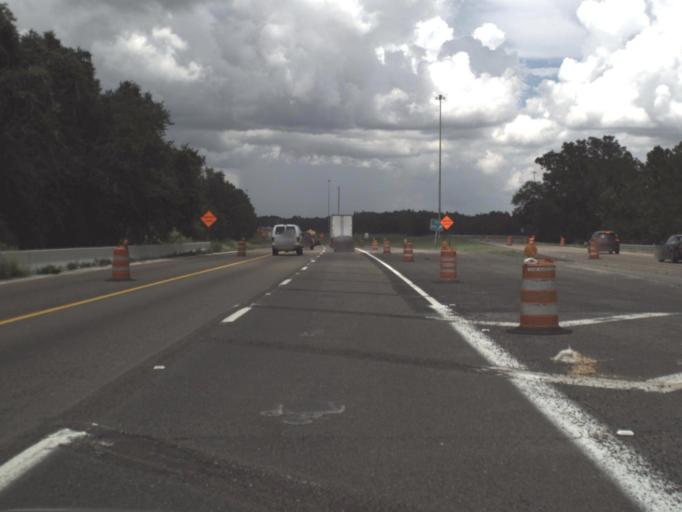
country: US
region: Florida
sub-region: Hillsborough County
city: Temple Terrace
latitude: 28.0708
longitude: -82.3526
